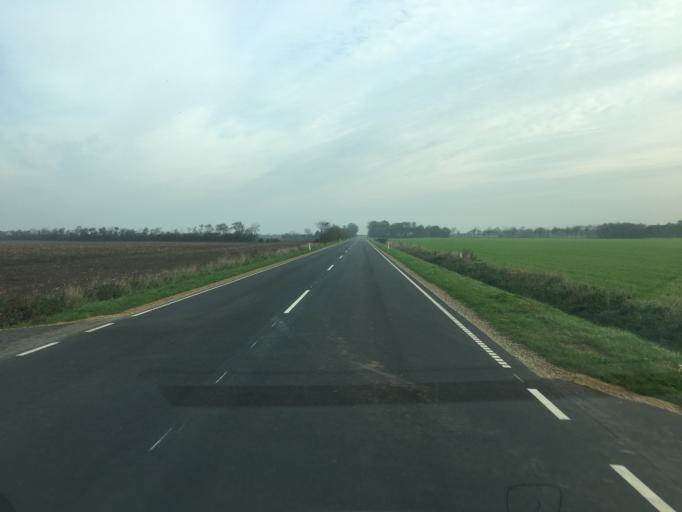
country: DK
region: South Denmark
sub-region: Tonder Kommune
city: Logumkloster
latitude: 55.0745
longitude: 8.9762
